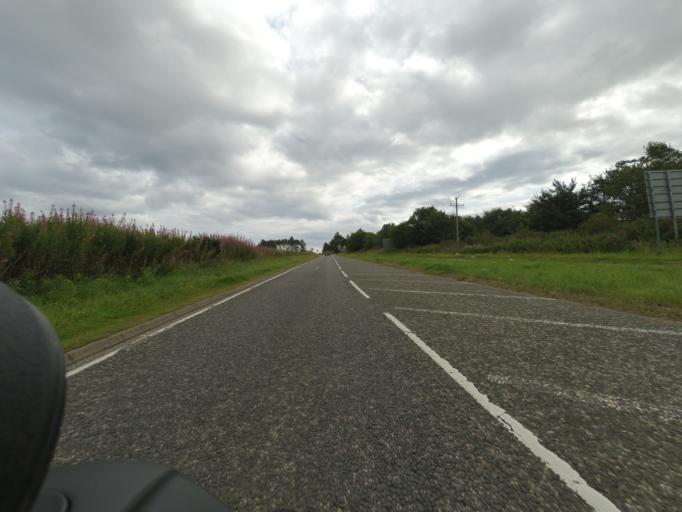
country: GB
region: Scotland
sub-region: Aberdeenshire
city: Stonehaven
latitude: 56.9490
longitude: -2.2239
